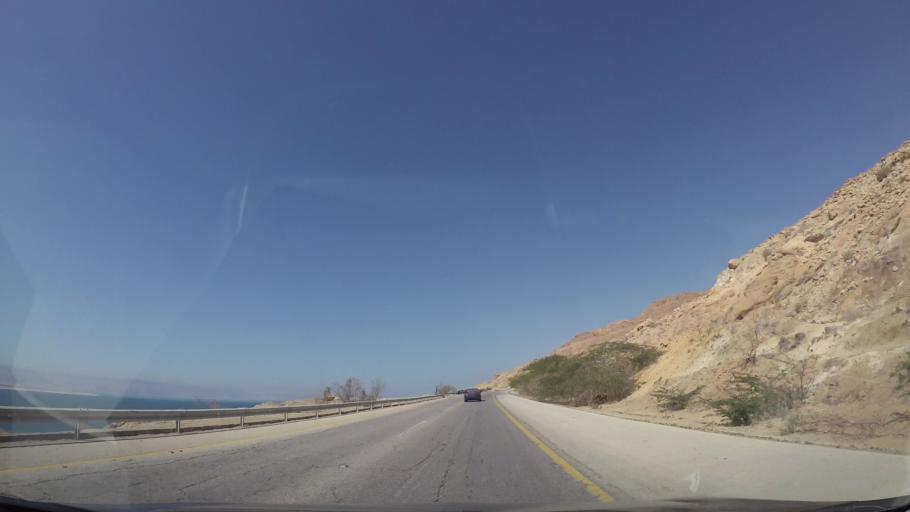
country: JO
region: Karak
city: Al Qasr
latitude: 31.3544
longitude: 35.5479
